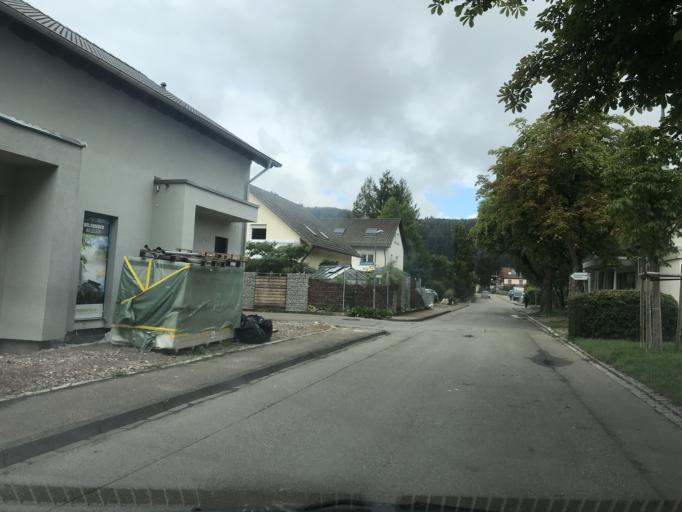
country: DE
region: Baden-Wuerttemberg
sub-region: Freiburg Region
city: Schopfheim
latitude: 47.6570
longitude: 7.8394
